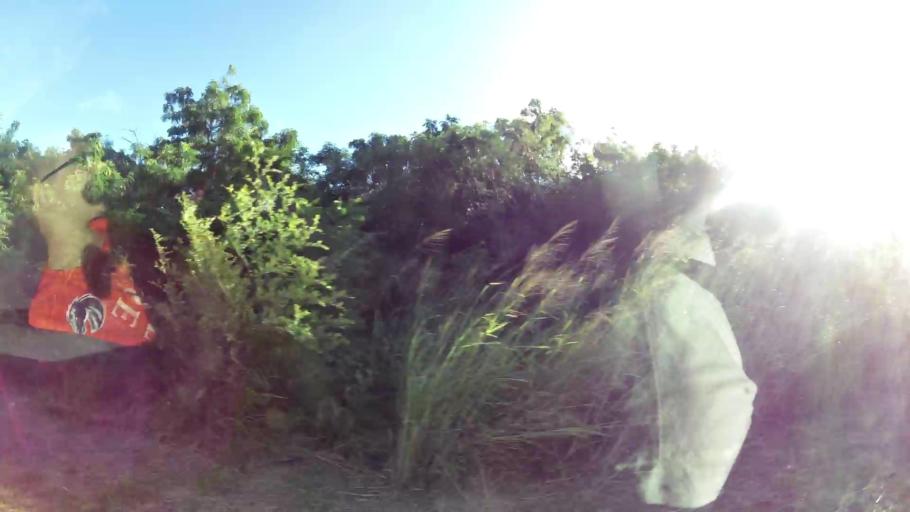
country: AG
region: Saint George
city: Piggotts
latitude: 17.1262
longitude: -61.7917
